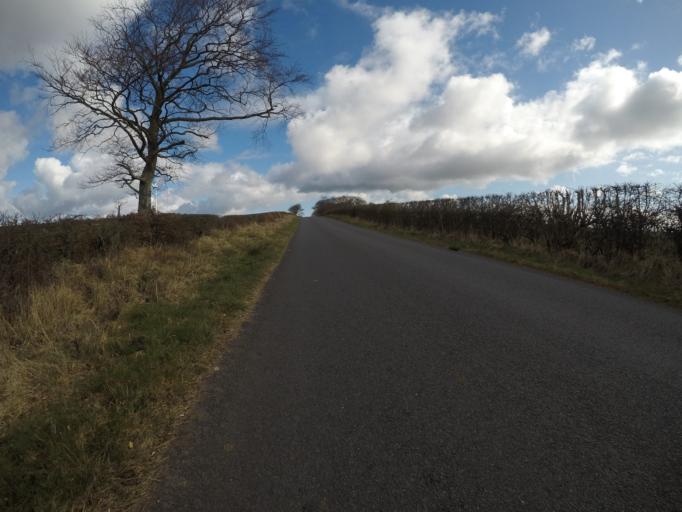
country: GB
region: Scotland
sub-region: North Ayrshire
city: Kilwinning
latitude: 55.6773
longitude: -4.6557
